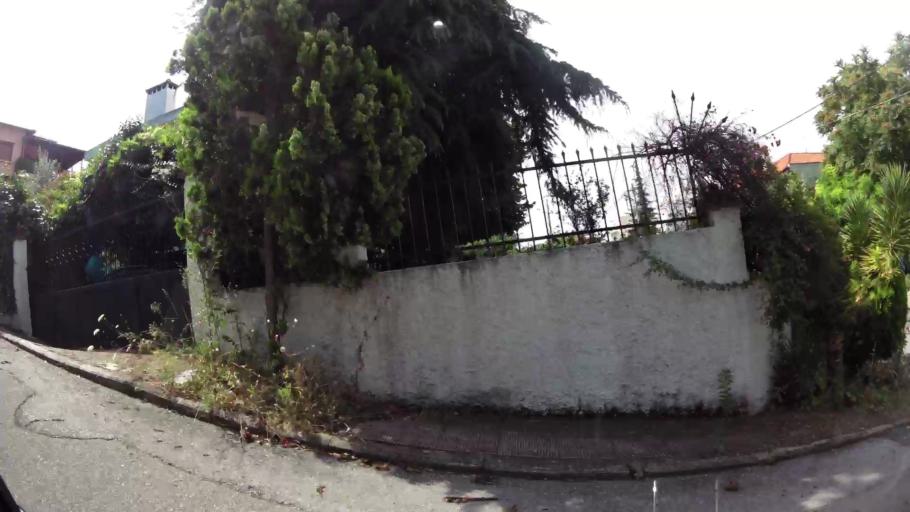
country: GR
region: Central Macedonia
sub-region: Nomos Thessalonikis
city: Panorama
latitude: 40.5790
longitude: 23.0194
